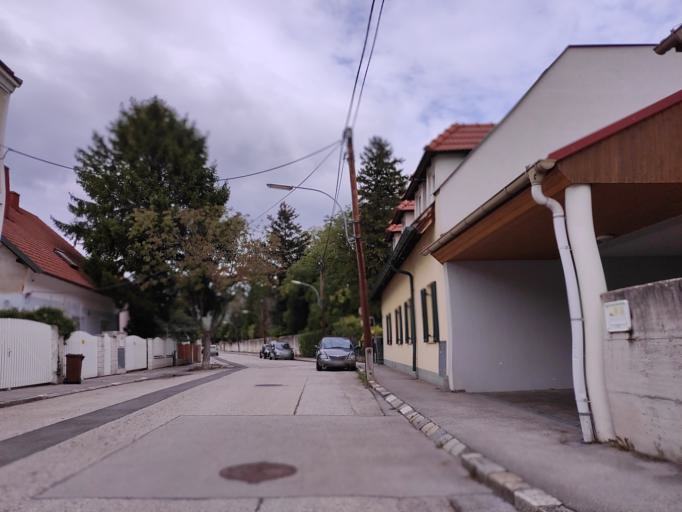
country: AT
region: Lower Austria
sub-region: Politischer Bezirk Baden
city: Baden
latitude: 48.0041
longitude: 16.2492
